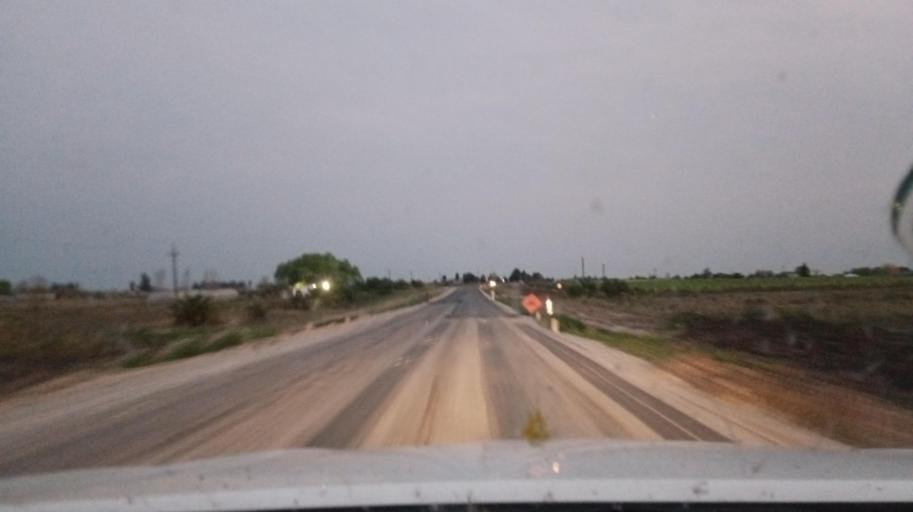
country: UY
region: Canelones
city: Sauce
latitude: -34.5707
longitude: -56.1012
